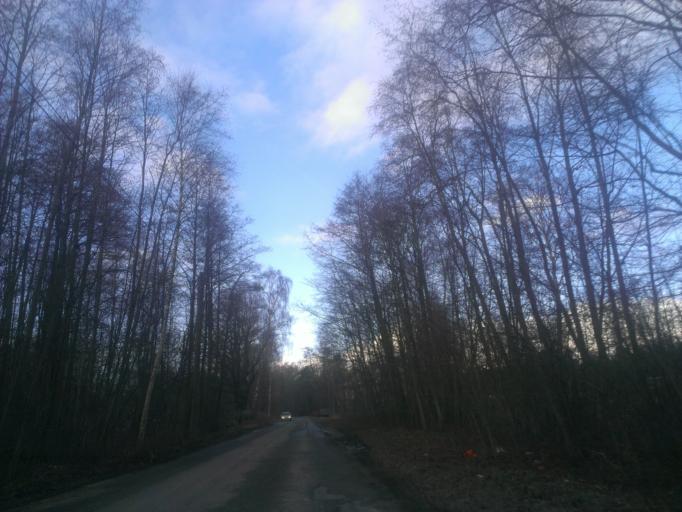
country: LV
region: Riga
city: Daugavgriva
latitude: 57.0599
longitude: 24.0572
